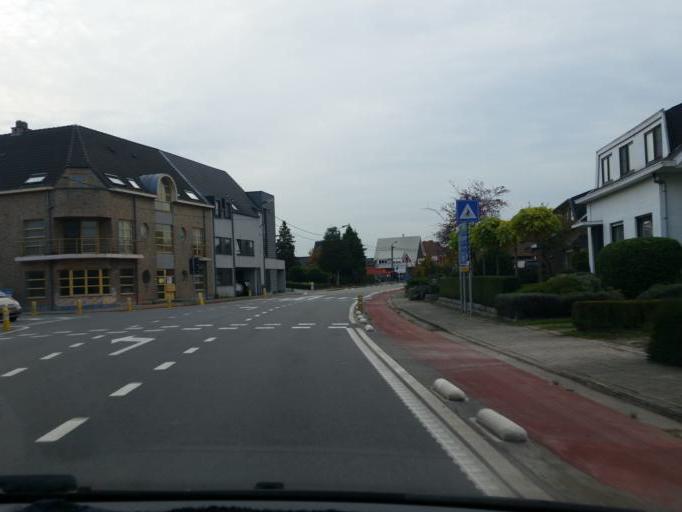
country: BE
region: Flanders
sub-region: Provincie Antwerpen
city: Sint-Katelijne-Waver
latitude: 51.0724
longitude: 4.5741
